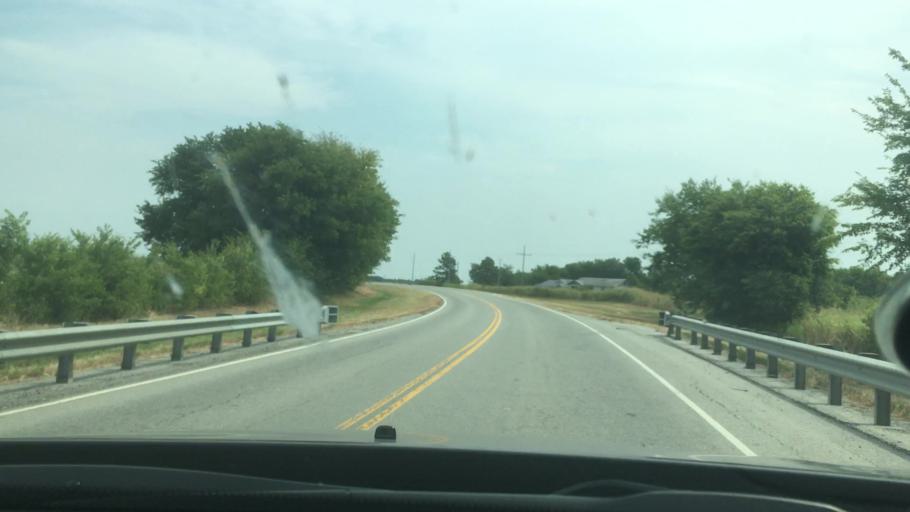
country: US
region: Oklahoma
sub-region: Coal County
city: Coalgate
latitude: 34.4985
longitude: -96.4092
